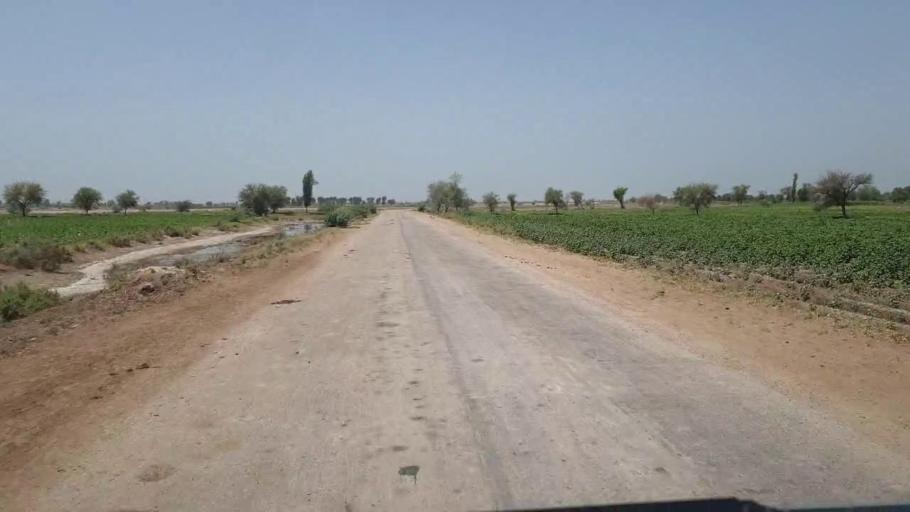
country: PK
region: Sindh
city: Nawabshah
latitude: 26.3688
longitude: 68.4137
